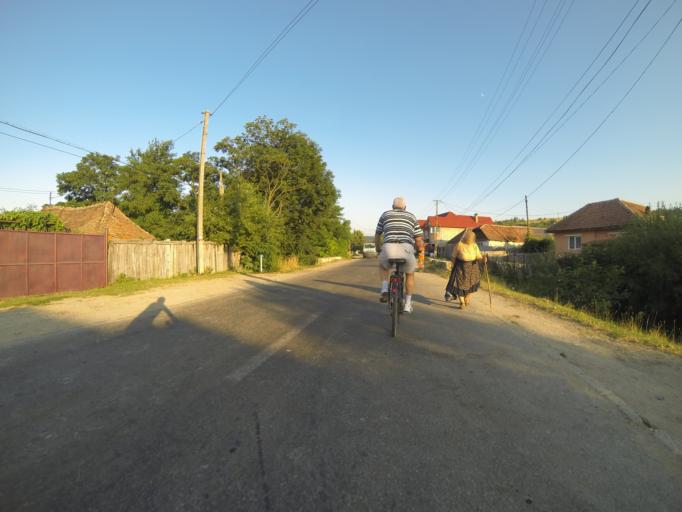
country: RO
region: Brasov
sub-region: Comuna Sinca Veche
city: Sinca Veche
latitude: 45.7547
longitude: 25.1768
